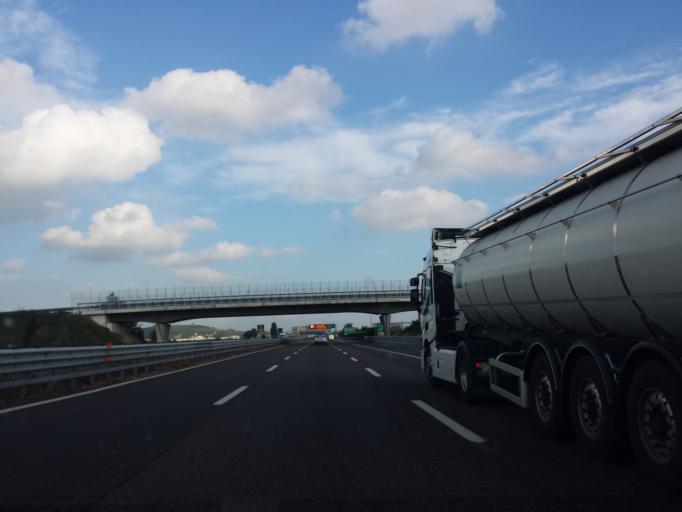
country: IT
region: Veneto
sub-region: Provincia di Verona
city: Soave
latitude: 45.4122
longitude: 11.2212
